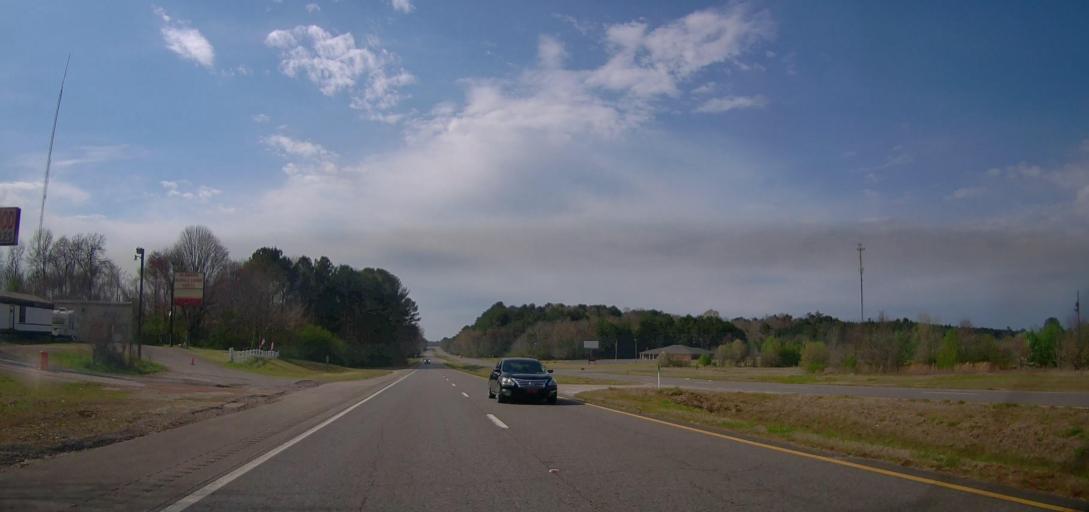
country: US
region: Alabama
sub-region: Jefferson County
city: Adamsville
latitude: 33.6017
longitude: -86.9498
